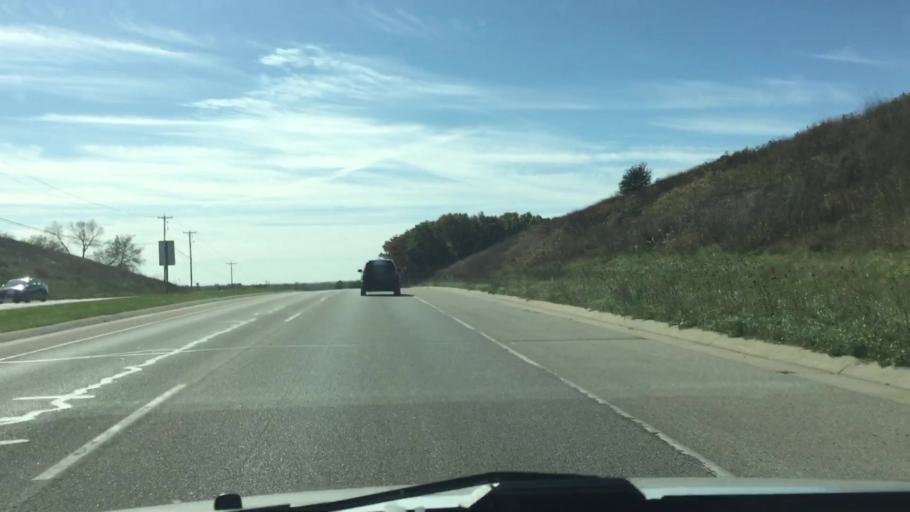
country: US
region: Wisconsin
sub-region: Waukesha County
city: Pewaukee
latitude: 43.1091
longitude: -88.2449
